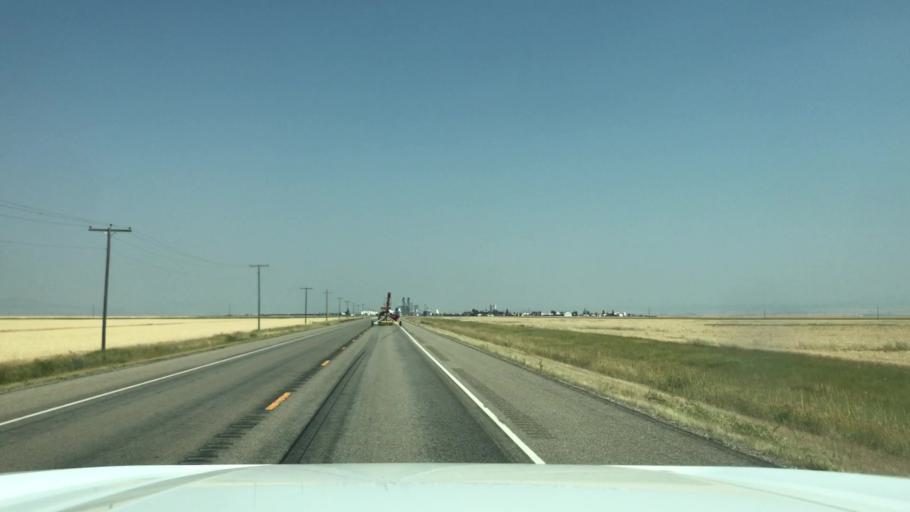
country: US
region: Montana
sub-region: Judith Basin County
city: Stanford
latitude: 47.0552
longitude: -109.9339
